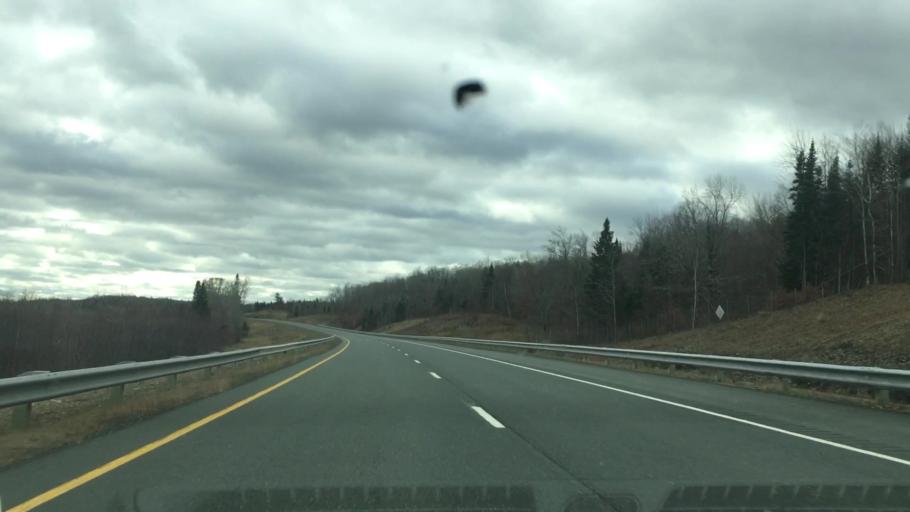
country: US
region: Maine
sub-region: Aroostook County
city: Fort Fairfield
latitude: 46.6487
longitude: -67.7427
